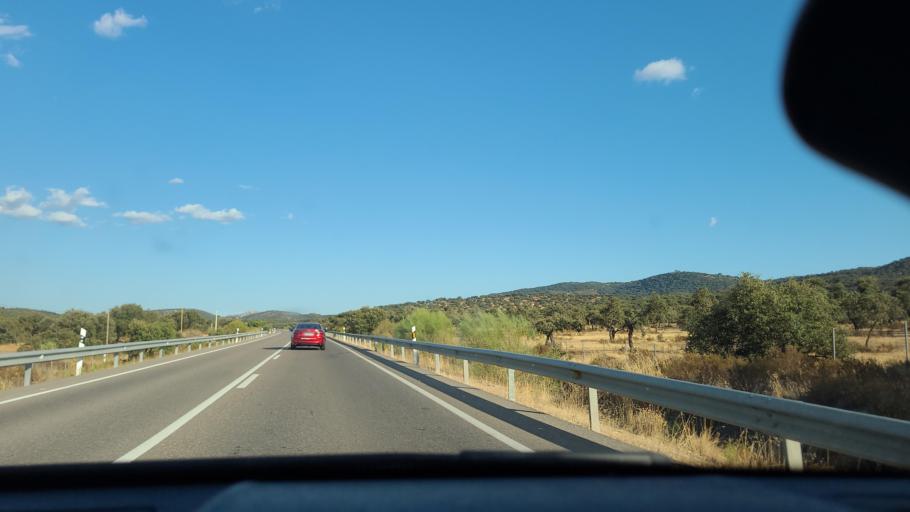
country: ES
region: Andalusia
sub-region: Province of Cordoba
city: Belmez
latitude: 38.2093
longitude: -5.1327
